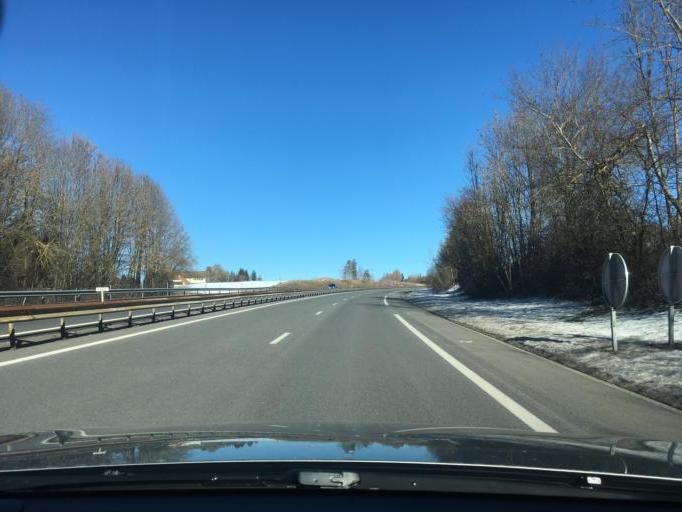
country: FR
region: Rhone-Alpes
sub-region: Departement de la Haute-Savoie
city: Evires
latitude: 46.0377
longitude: 6.2415
